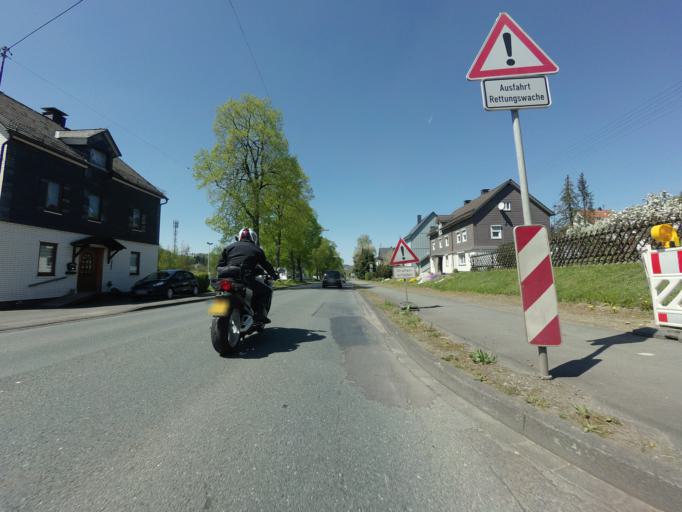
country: DE
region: North Rhine-Westphalia
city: Kreuztal
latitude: 50.9589
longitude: 8.0193
